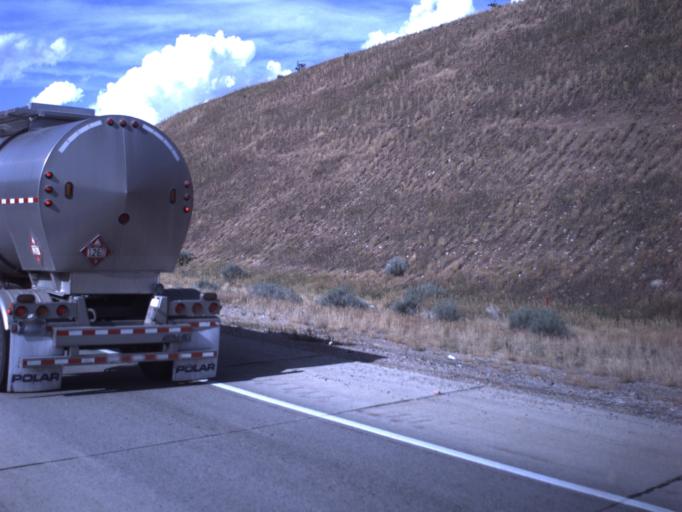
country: US
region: Utah
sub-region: Summit County
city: Park City
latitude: 40.5919
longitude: -111.4368
